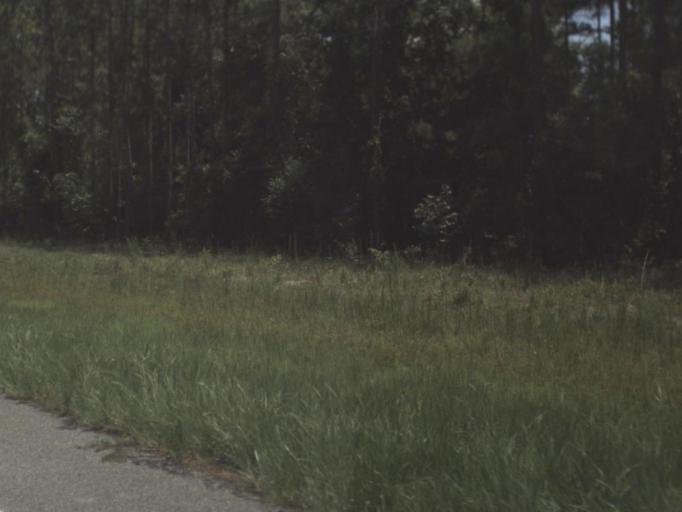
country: US
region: Florida
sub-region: Jefferson County
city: Monticello
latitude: 30.5474
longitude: -83.6351
